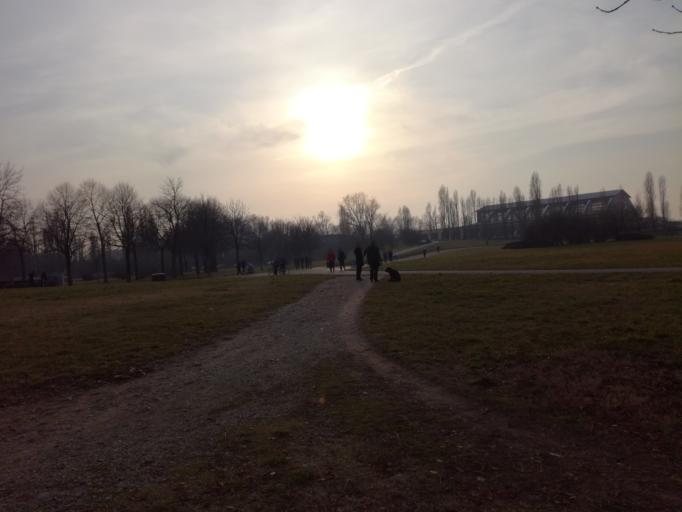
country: IT
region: Lombardy
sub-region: Citta metropolitana di Milano
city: Sesto San Giovanni
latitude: 45.5348
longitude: 9.2134
